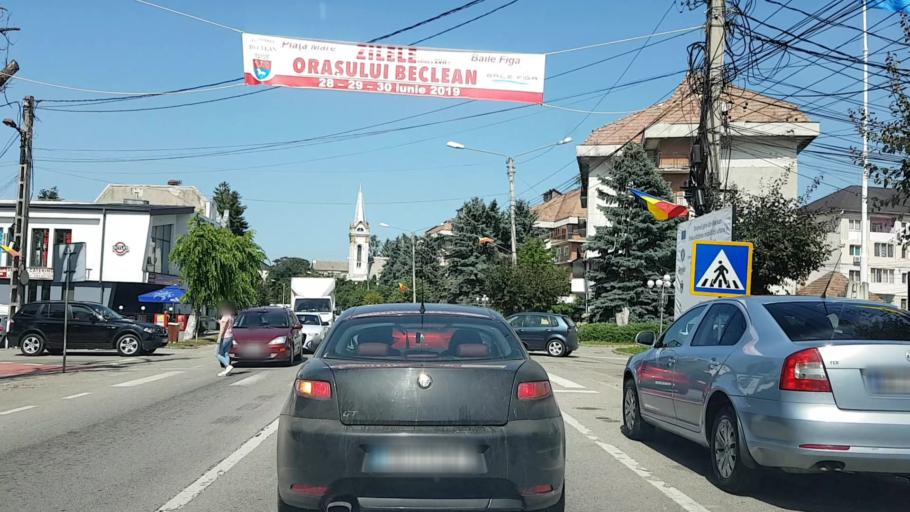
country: RO
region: Bistrita-Nasaud
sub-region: Comuna Beclean
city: Beclean
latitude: 47.1799
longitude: 24.1797
